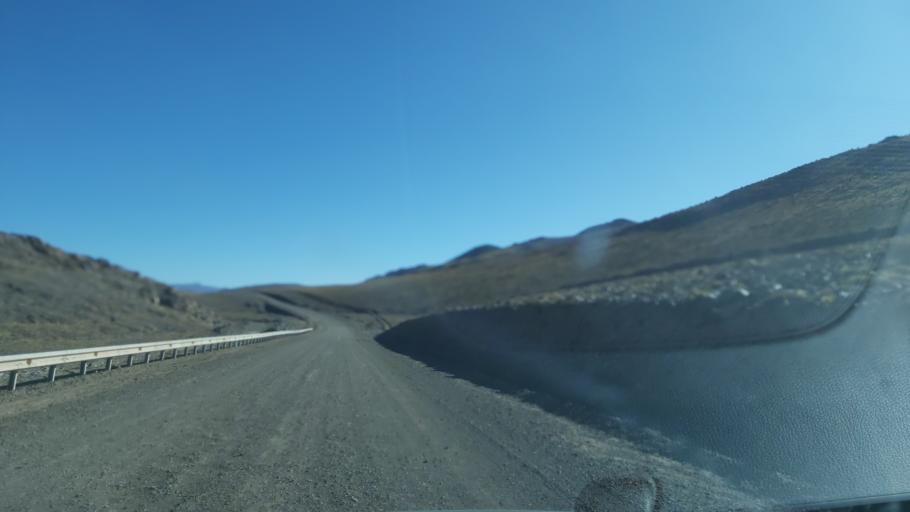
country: CL
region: Atacama
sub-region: Provincia de Chanaral
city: Diego de Almagro
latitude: -26.4328
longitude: -69.2819
